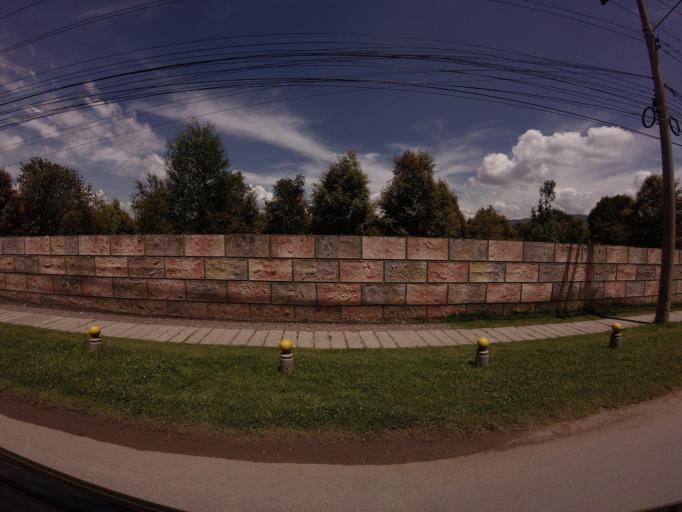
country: CO
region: Cundinamarca
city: Sopo
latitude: 4.9454
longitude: -73.9599
